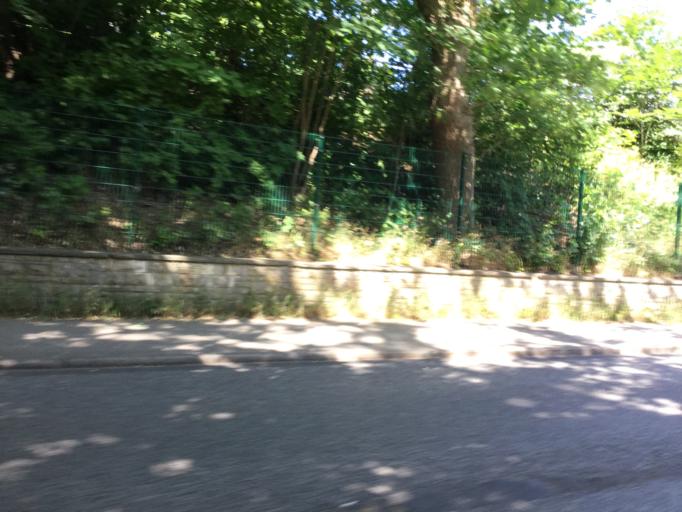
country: DE
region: Hamburg
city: Bergstedt
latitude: 53.6511
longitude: 10.1638
